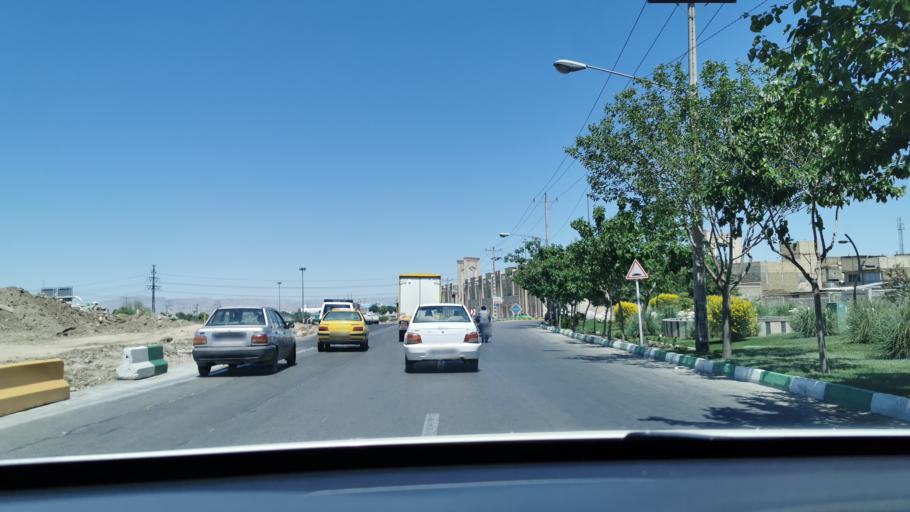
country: IR
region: Razavi Khorasan
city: Mashhad
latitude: 36.2604
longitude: 59.6483
